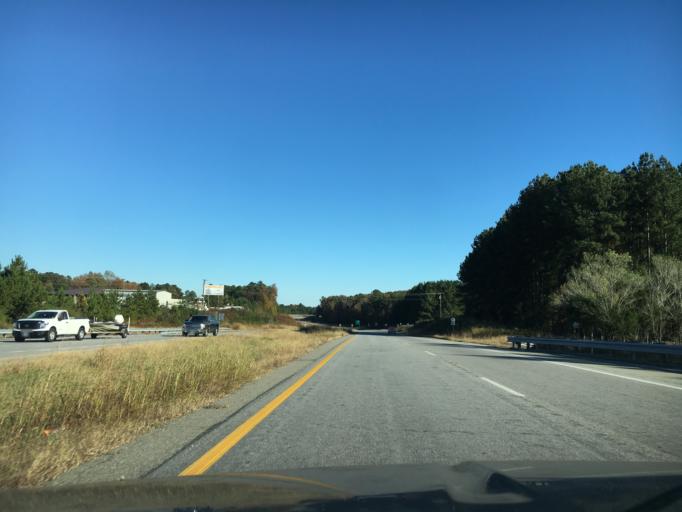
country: US
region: Virginia
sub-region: Mecklenburg County
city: Clarksville
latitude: 36.6115
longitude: -78.5893
